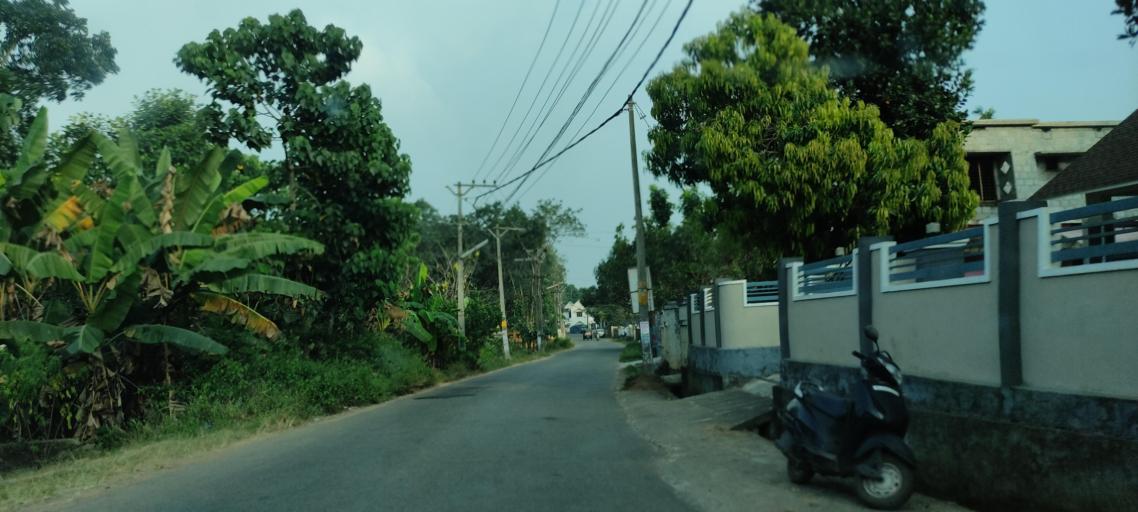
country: IN
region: Kerala
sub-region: Pattanamtitta
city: Adur
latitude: 9.0904
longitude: 76.7493
